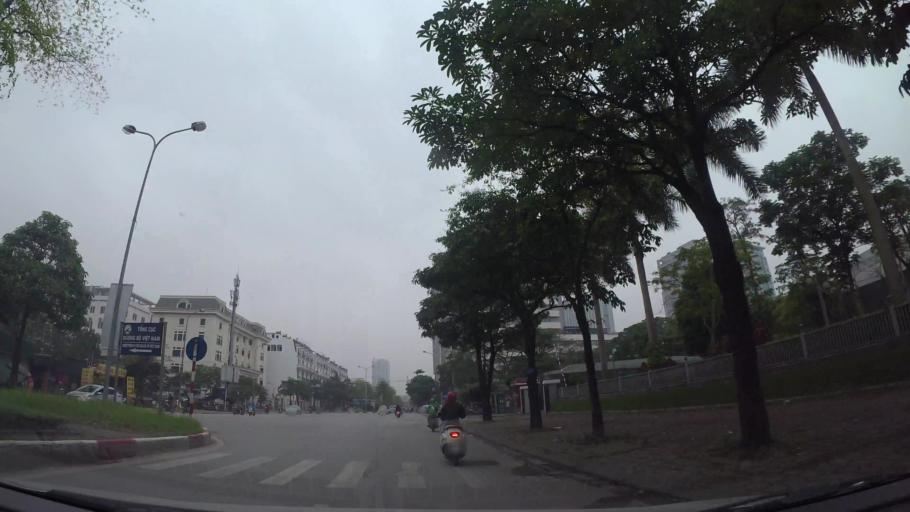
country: VN
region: Ha Noi
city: Cau Giay
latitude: 21.0281
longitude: 105.7834
